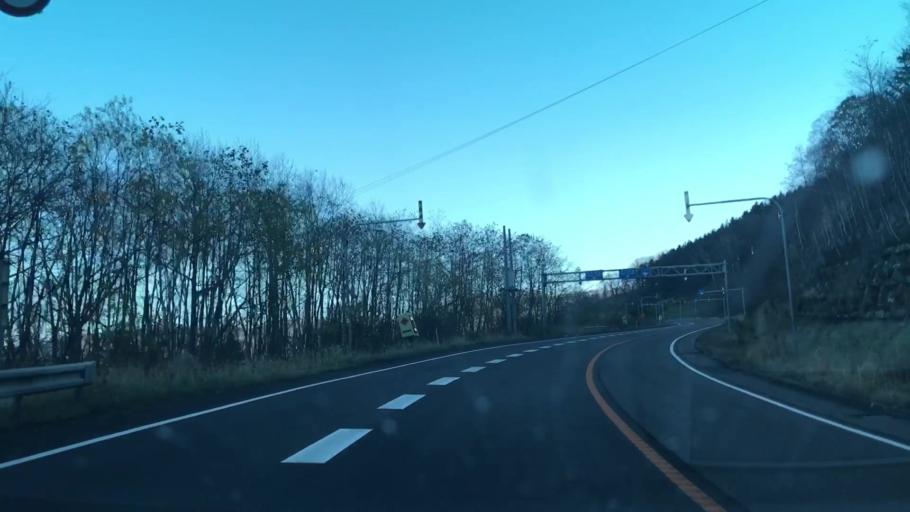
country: JP
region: Hokkaido
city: Otofuke
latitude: 42.9739
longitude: 142.8019
